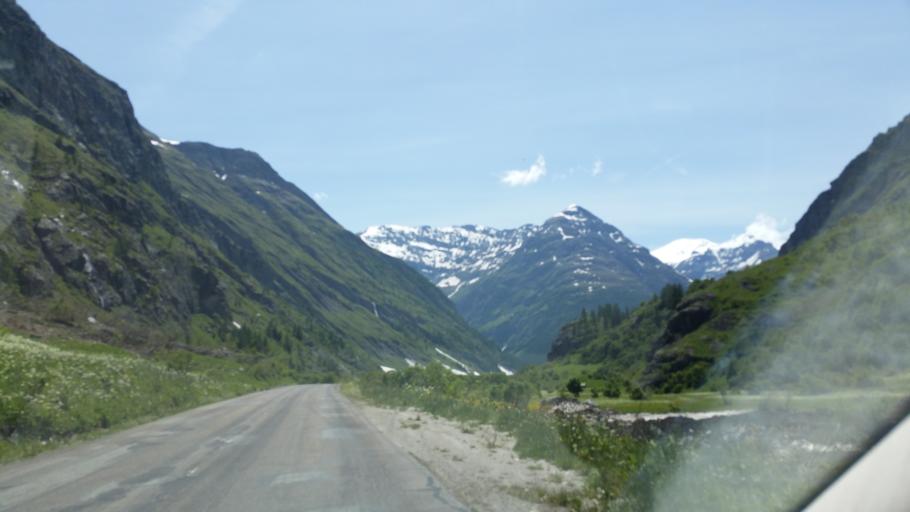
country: FR
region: Rhone-Alpes
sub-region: Departement de la Savoie
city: Val-d'Isere
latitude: 45.3557
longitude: 7.0296
